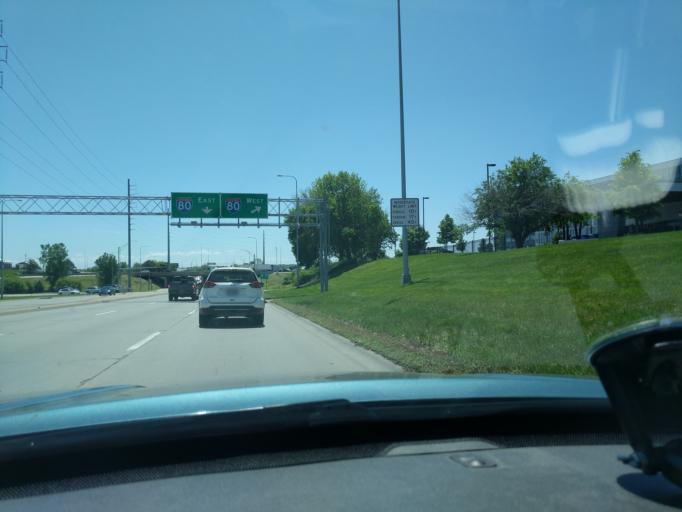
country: US
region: Nebraska
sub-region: Douglas County
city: Ralston
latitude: 41.2264
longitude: -96.0240
